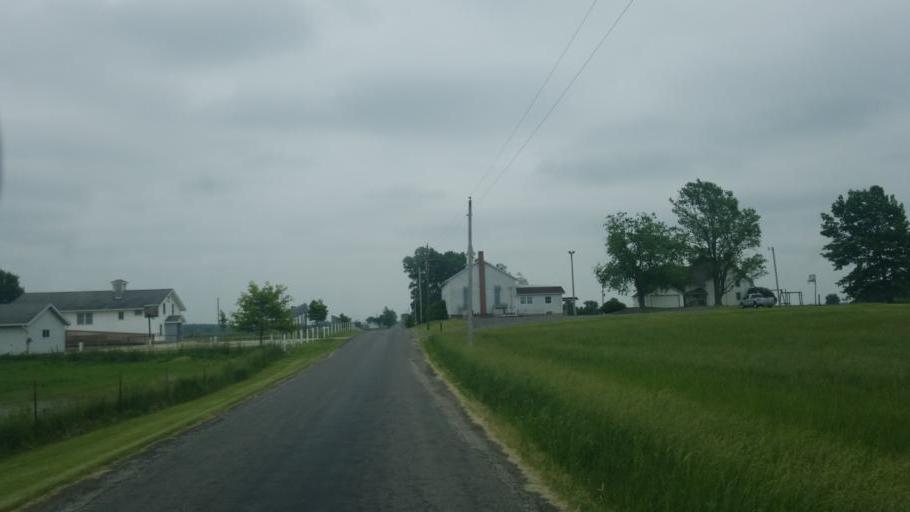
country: US
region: Indiana
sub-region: Elkhart County
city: Wakarusa
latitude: 41.4936
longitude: -86.0811
